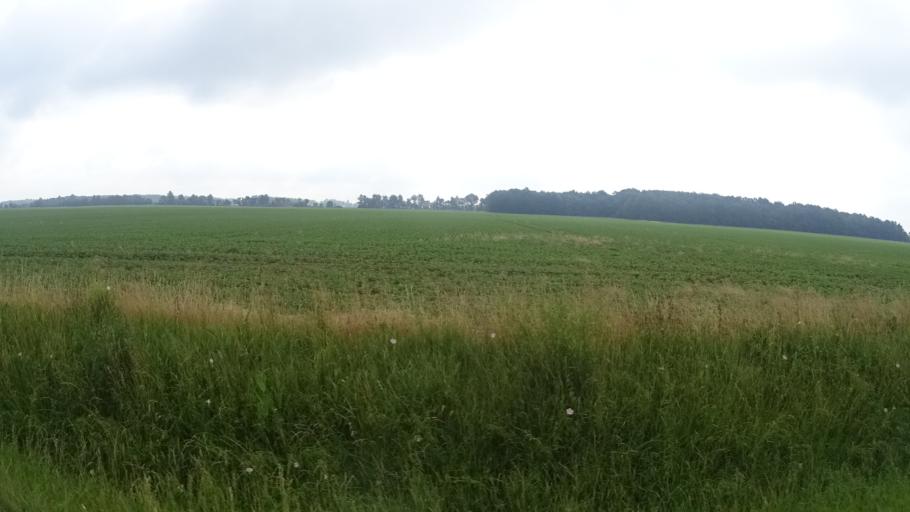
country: US
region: Ohio
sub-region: Huron County
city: Wakeman
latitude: 41.2809
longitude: -82.4917
